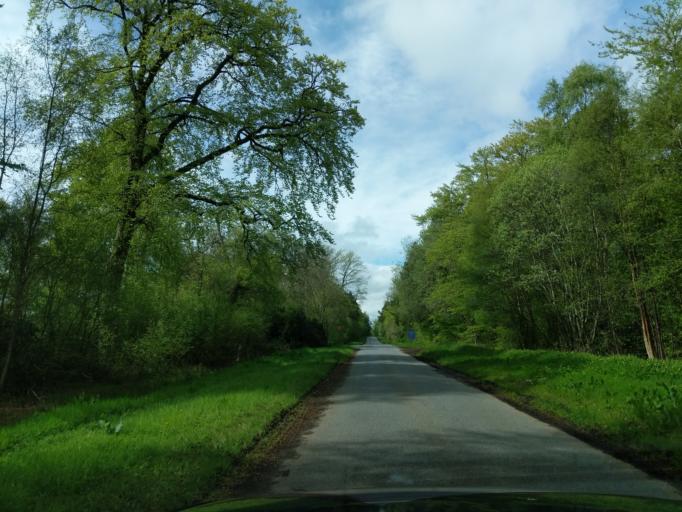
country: GB
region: Scotland
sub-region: The Scottish Borders
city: Saint Boswells
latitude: 55.6370
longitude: -2.5864
